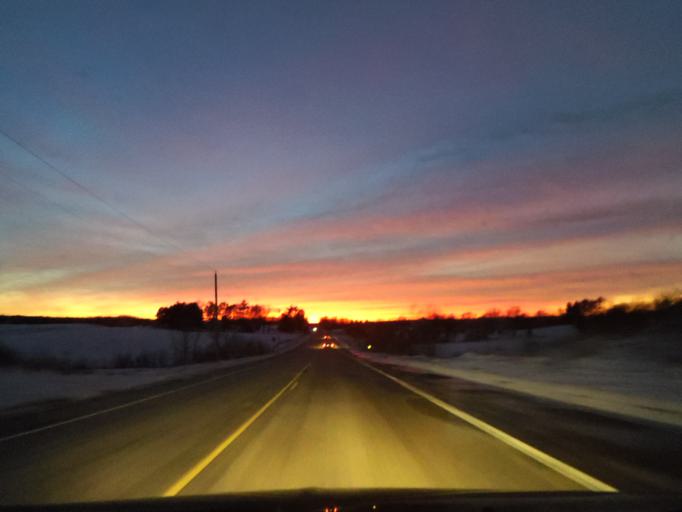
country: US
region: Minnesota
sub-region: Chisago County
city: Lindstrom
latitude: 45.3468
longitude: -92.8503
